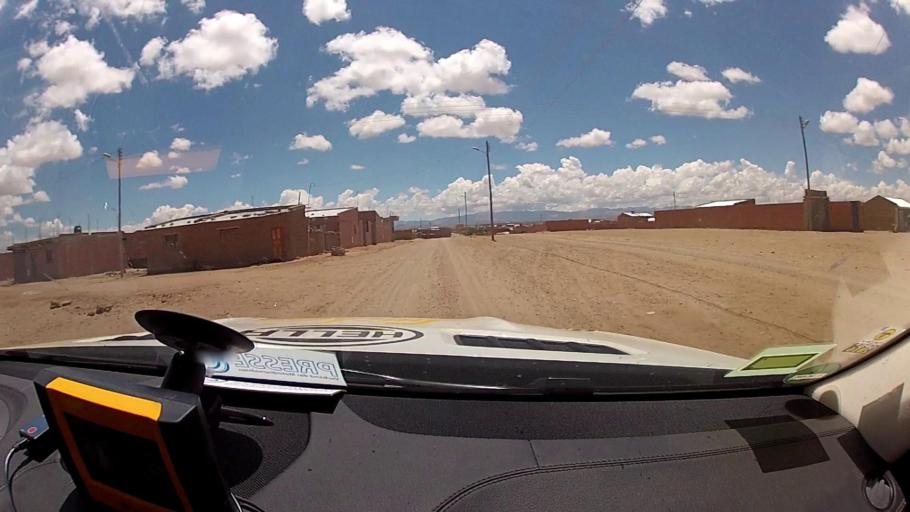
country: BO
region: Potosi
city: Villazon
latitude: -22.0804
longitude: -65.6089
